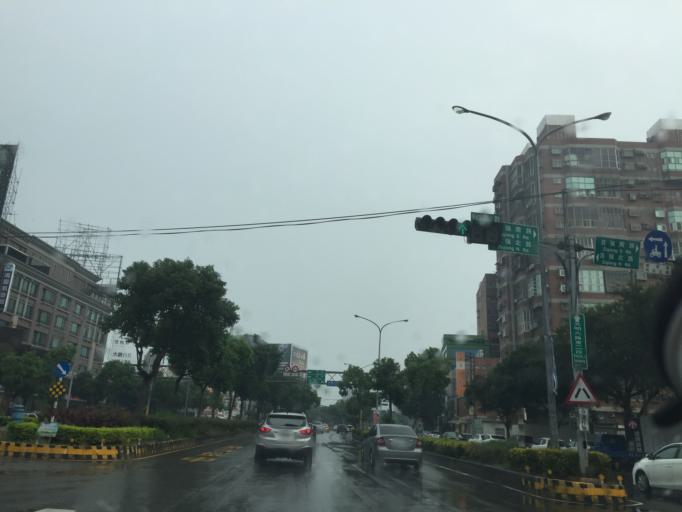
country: TW
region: Taiwan
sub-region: Hsinchu
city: Zhubei
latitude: 24.8197
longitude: 121.0284
